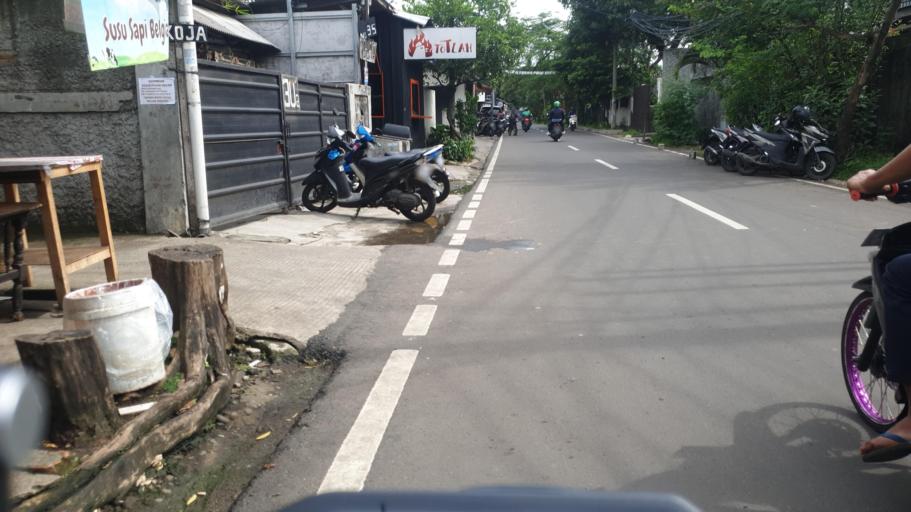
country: ID
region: West Java
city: Pamulang
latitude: -6.2935
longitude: 106.7923
